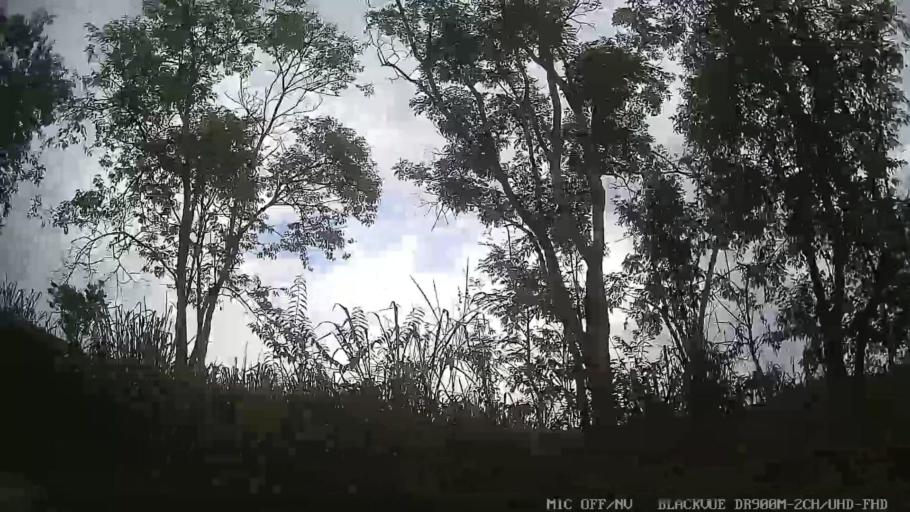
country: BR
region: Sao Paulo
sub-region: Aruja
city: Aruja
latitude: -23.4278
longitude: -46.2324
